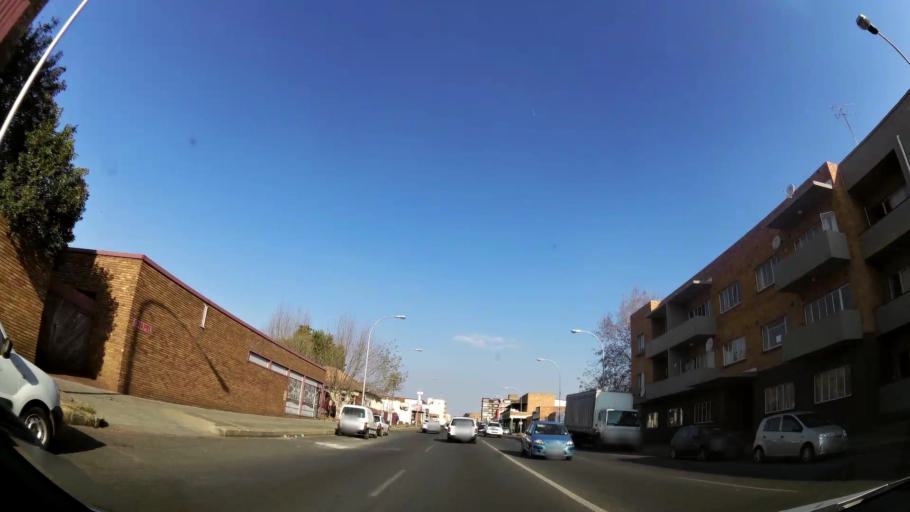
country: ZA
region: Gauteng
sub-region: Ekurhuleni Metropolitan Municipality
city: Brakpan
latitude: -26.2403
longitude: 28.3664
